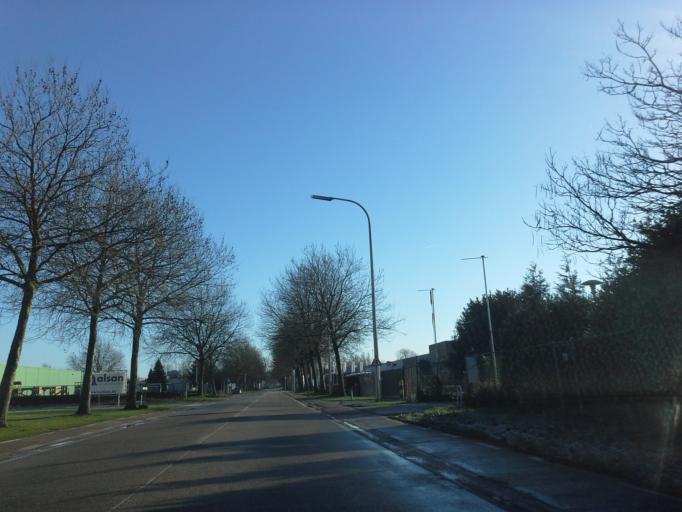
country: BE
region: Flanders
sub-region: Provincie Antwerpen
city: Herentals
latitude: 51.1592
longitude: 4.7937
